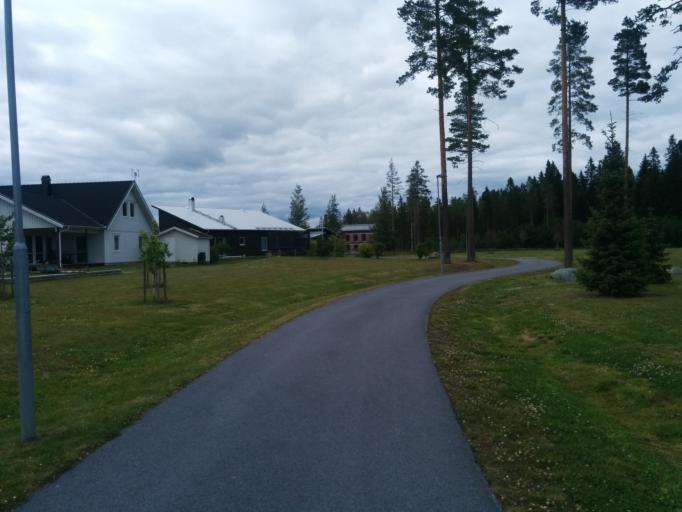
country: SE
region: Vaesterbotten
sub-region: Umea Kommun
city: Ersmark
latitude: 63.8038
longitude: 20.3741
